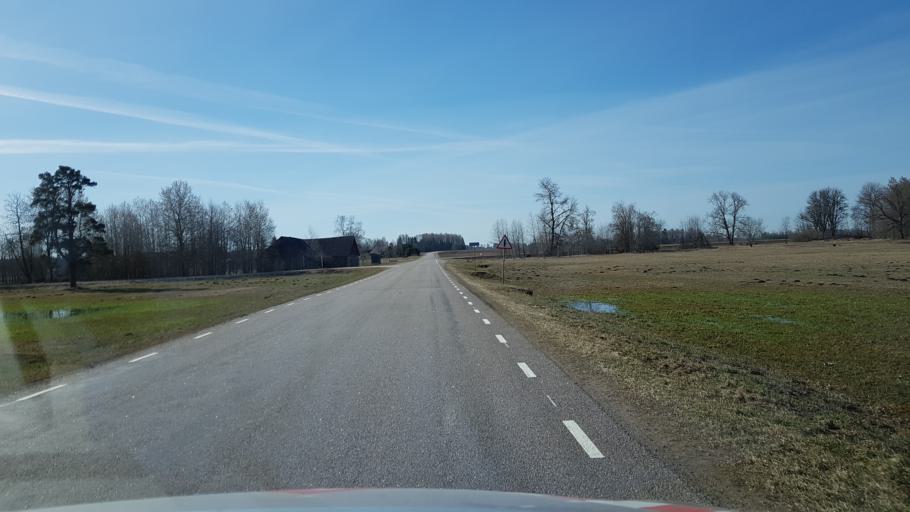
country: EE
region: Laeaene-Virumaa
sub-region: Vaeike-Maarja vald
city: Vaike-Maarja
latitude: 59.2135
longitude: 26.3334
